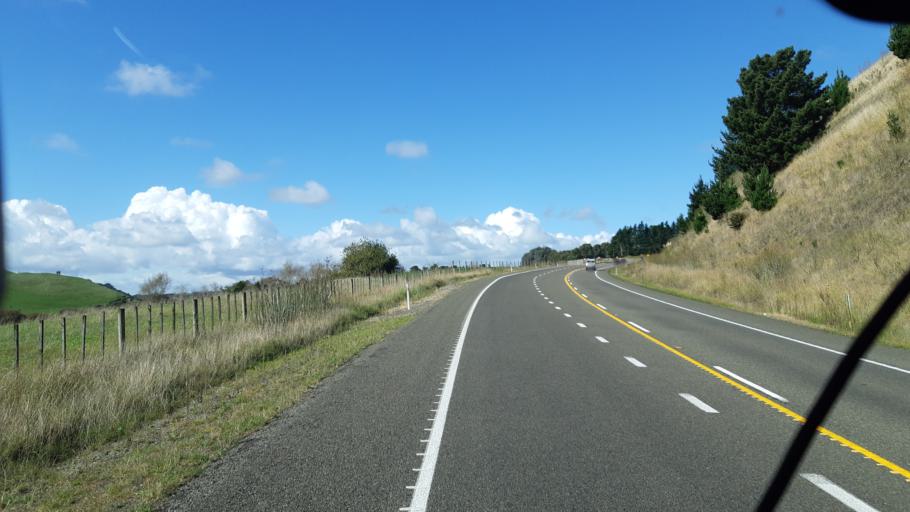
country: NZ
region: Manawatu-Wanganui
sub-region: Wanganui District
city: Wanganui
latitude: -39.9696
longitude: 175.1074
